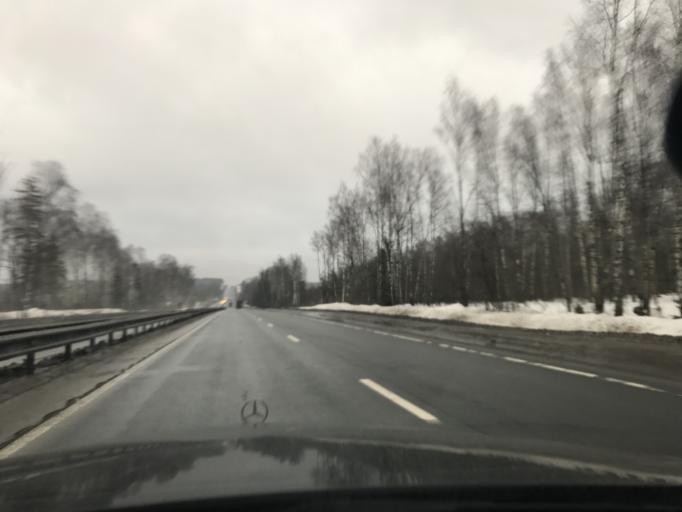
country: RU
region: Vladimir
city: Melekhovo
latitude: 56.2095
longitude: 41.2690
